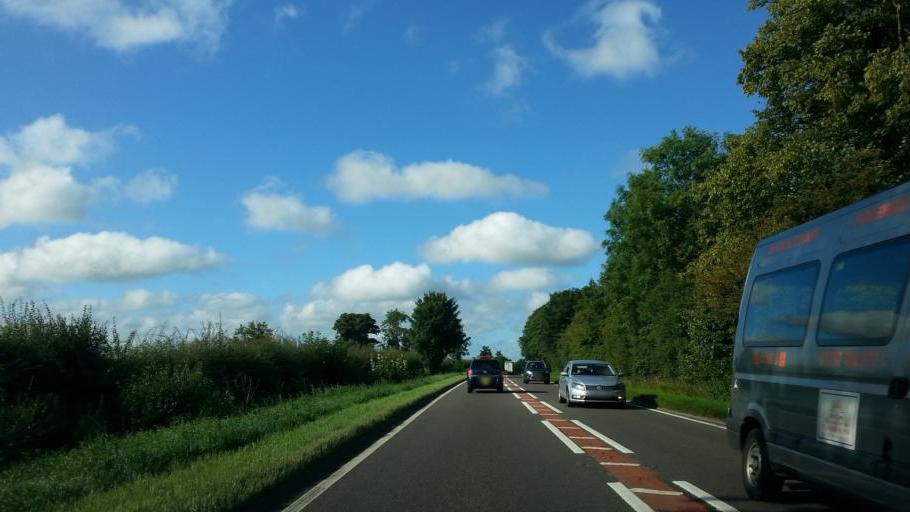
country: GB
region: England
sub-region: Northamptonshire
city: Earls Barton
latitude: 52.3041
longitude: -0.8218
